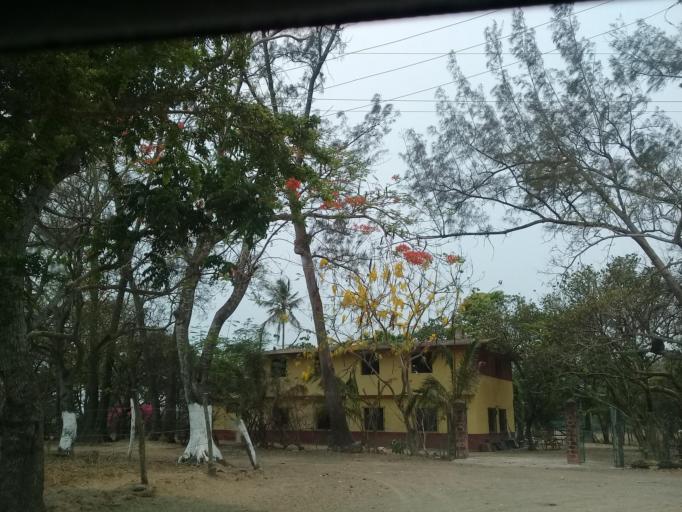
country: MX
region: Veracruz
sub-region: Veracruz
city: Las Amapolas
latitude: 19.1471
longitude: -96.2112
